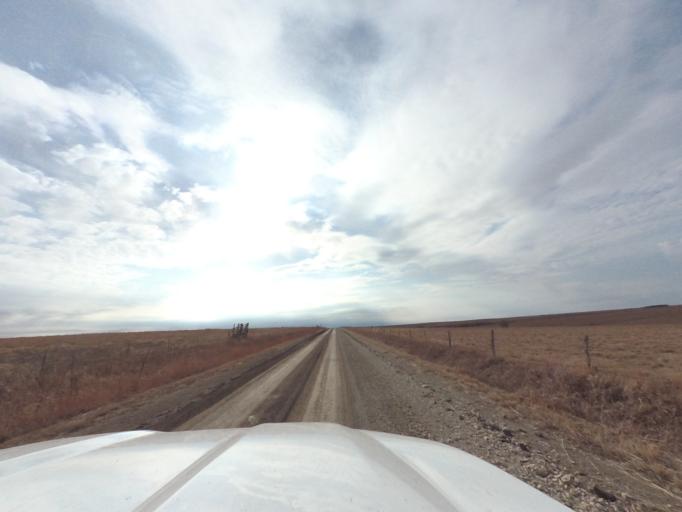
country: US
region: Kansas
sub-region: Chase County
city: Cottonwood Falls
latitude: 38.2333
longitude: -96.7306
